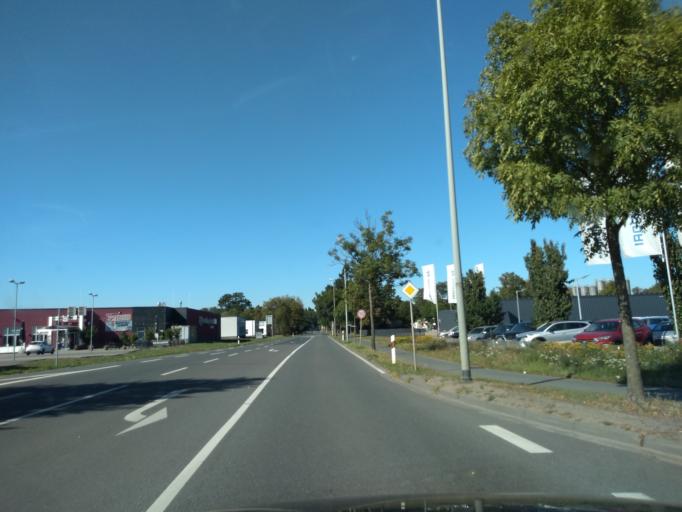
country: DE
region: North Rhine-Westphalia
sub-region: Regierungsbezirk Dusseldorf
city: Dinslaken
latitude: 51.5545
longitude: 6.7487
